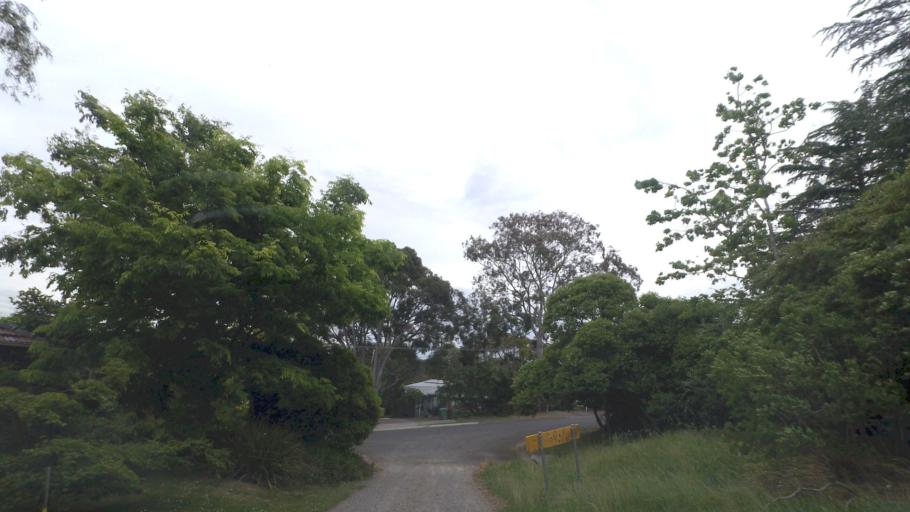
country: AU
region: Victoria
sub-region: Maroondah
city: Croydon North
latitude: -37.7914
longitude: 145.2942
